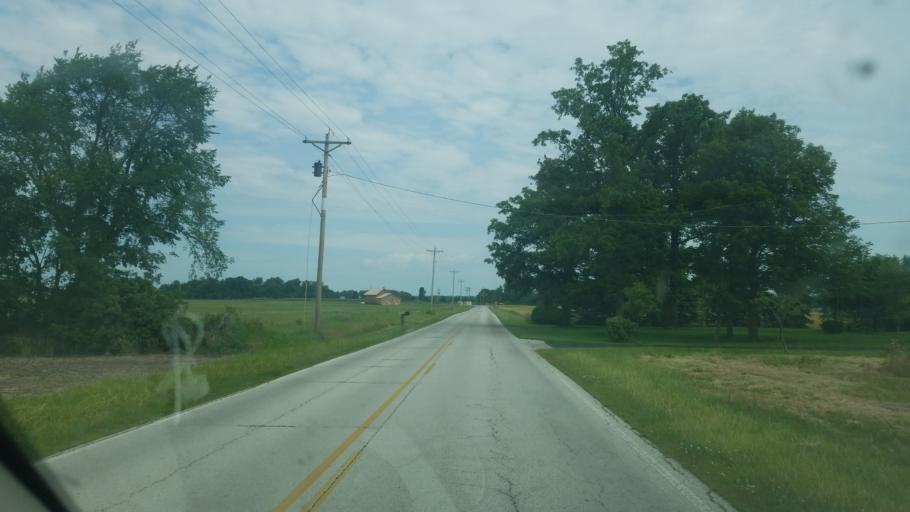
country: US
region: Ohio
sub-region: Seneca County
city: Fostoria
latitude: 41.1223
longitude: -83.4787
